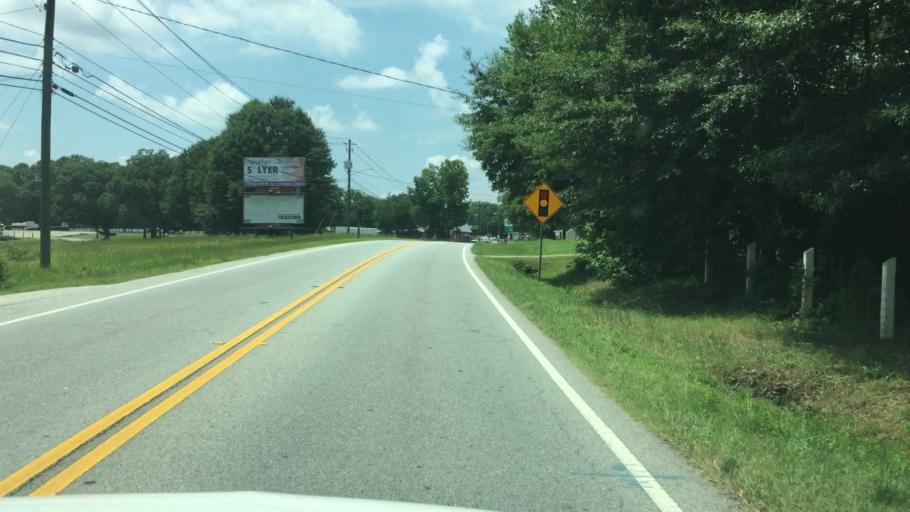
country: US
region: Georgia
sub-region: Barrow County
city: Auburn
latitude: 34.0038
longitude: -83.8086
